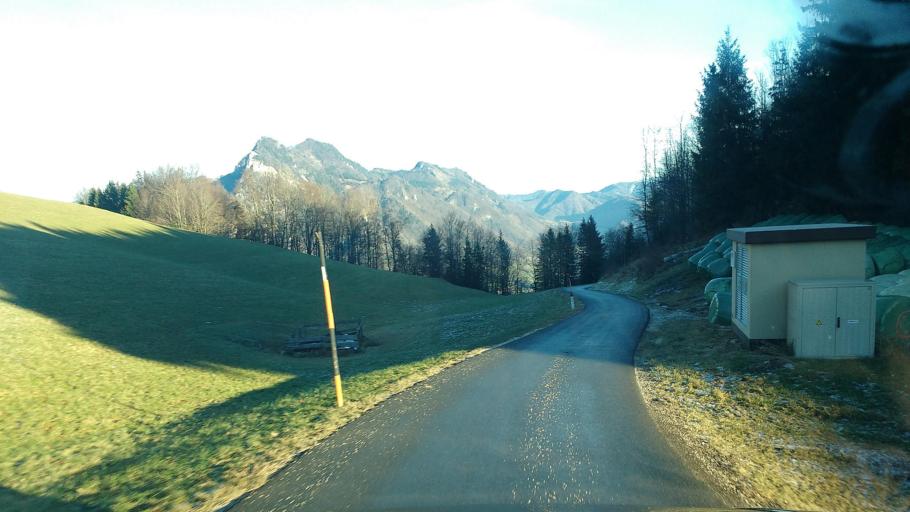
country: AT
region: Upper Austria
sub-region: Politischer Bezirk Kirchdorf an der Krems
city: Micheldorf in Oberoesterreich
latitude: 47.8970
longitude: 14.2145
